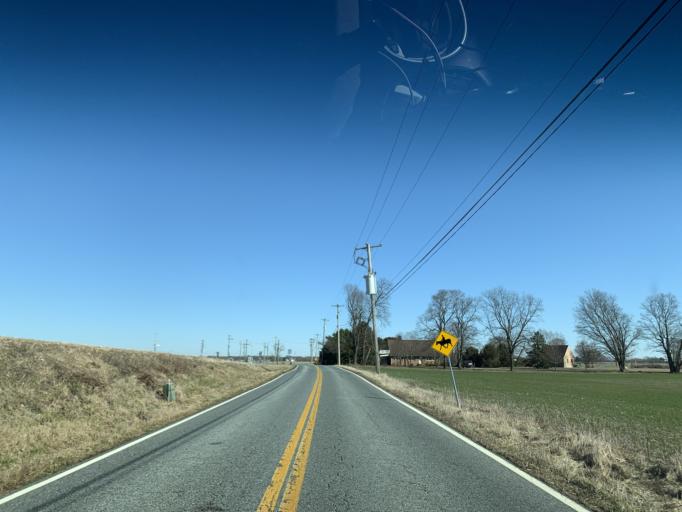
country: US
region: Maryland
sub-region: Cecil County
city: Elkton
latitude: 39.4897
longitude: -75.8587
